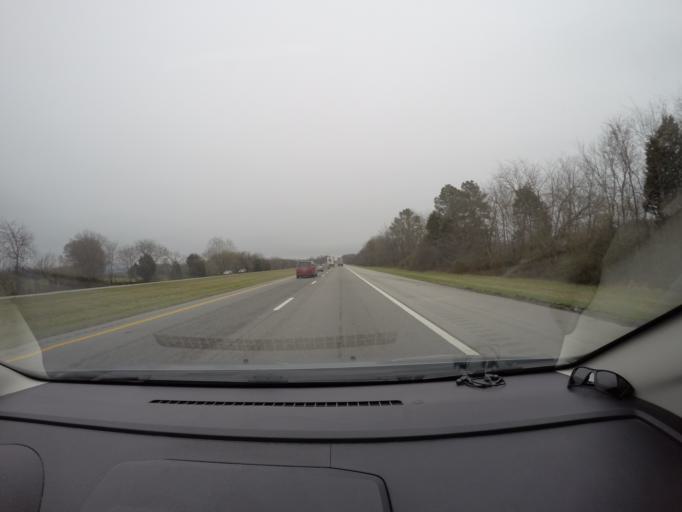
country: US
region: Tennessee
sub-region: Coffee County
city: Manchester
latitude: 35.3771
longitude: -85.9759
